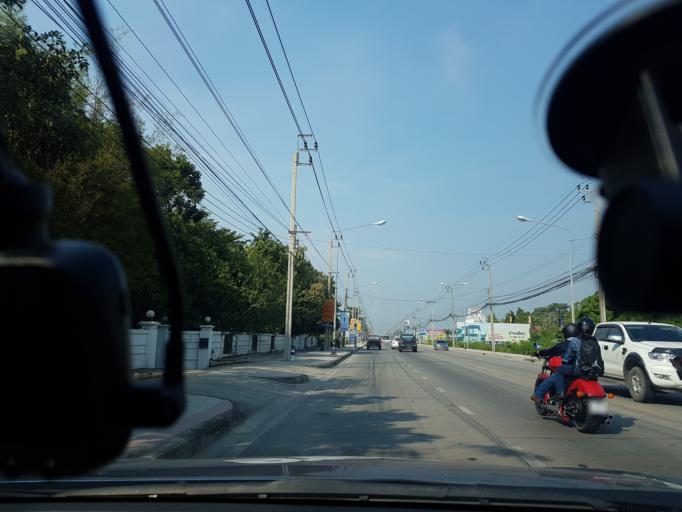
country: TH
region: Pathum Thani
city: Lam Luk Ka
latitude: 13.8899
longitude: 100.7221
